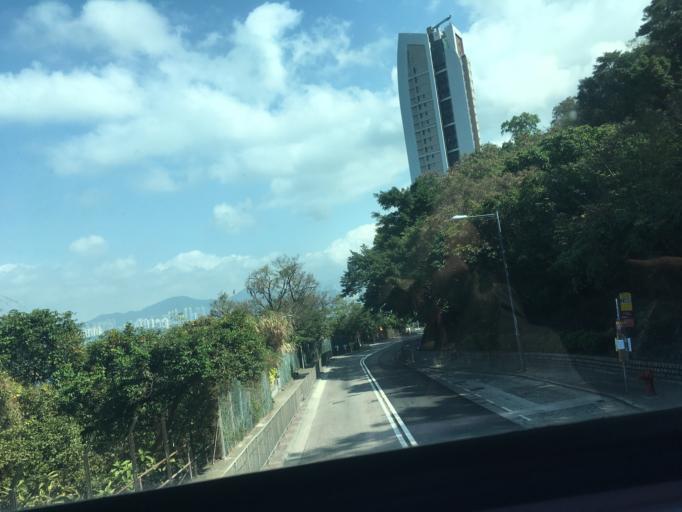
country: HK
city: Hong Kong
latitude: 22.2801
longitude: 114.1184
